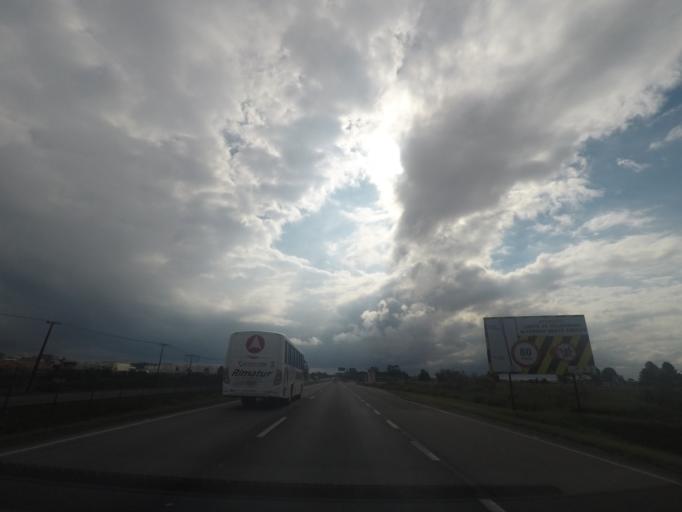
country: BR
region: Parana
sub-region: Sao Jose Dos Pinhais
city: Sao Jose dos Pinhais
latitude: -25.5137
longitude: -49.1229
